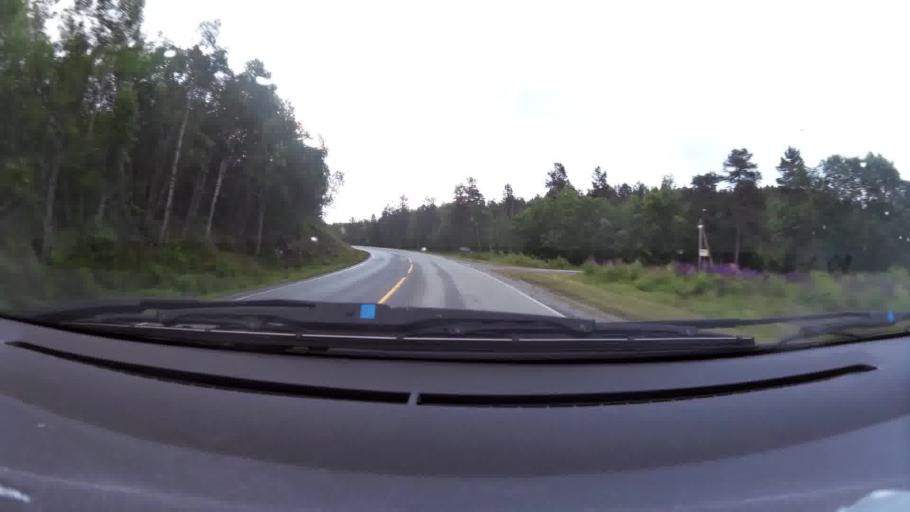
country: NO
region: More og Romsdal
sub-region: Molde
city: Molde
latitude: 62.7838
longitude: 7.3059
